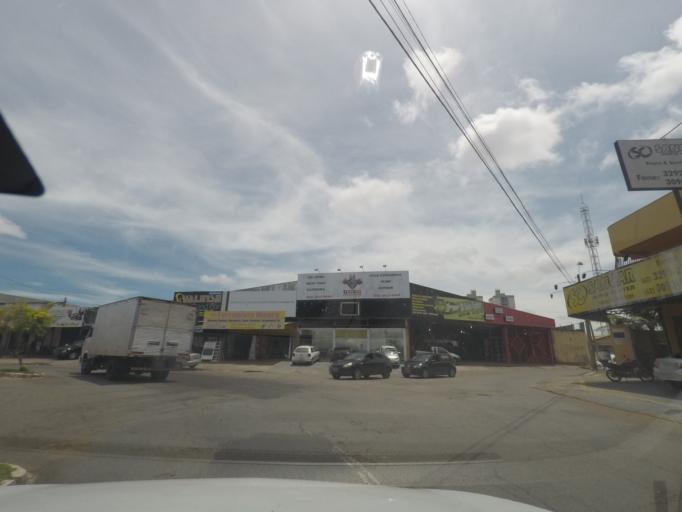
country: BR
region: Goias
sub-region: Goiania
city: Goiania
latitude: -16.6858
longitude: -49.2969
